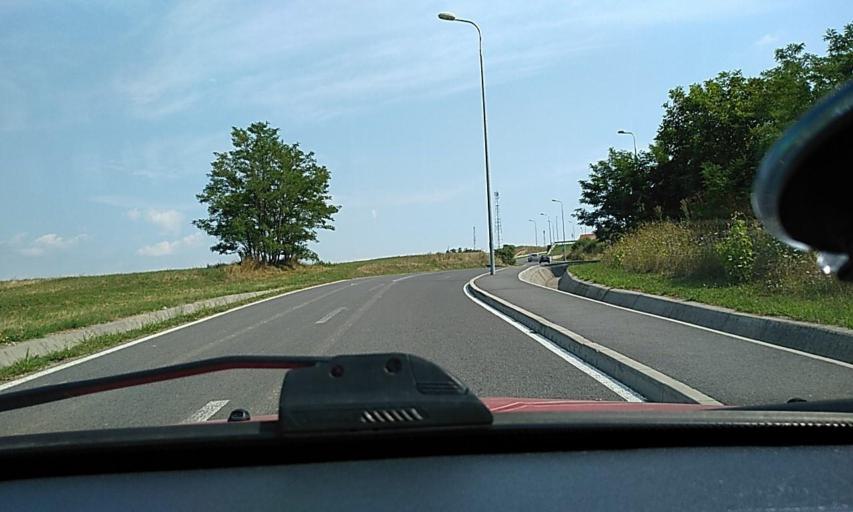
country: RO
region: Brasov
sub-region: Oras Rupea
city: Rupea
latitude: 46.0369
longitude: 25.2105
